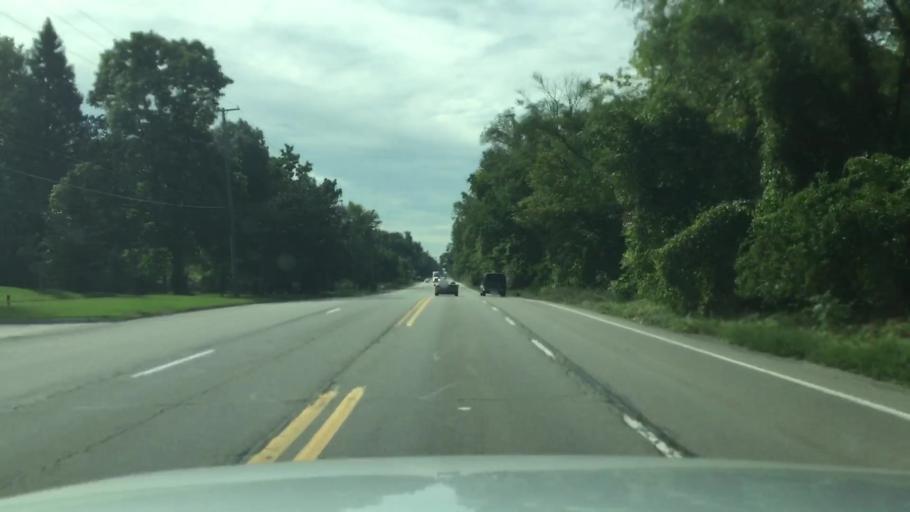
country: US
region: Michigan
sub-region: Wayne County
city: Belleville
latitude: 42.2564
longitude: -83.4866
